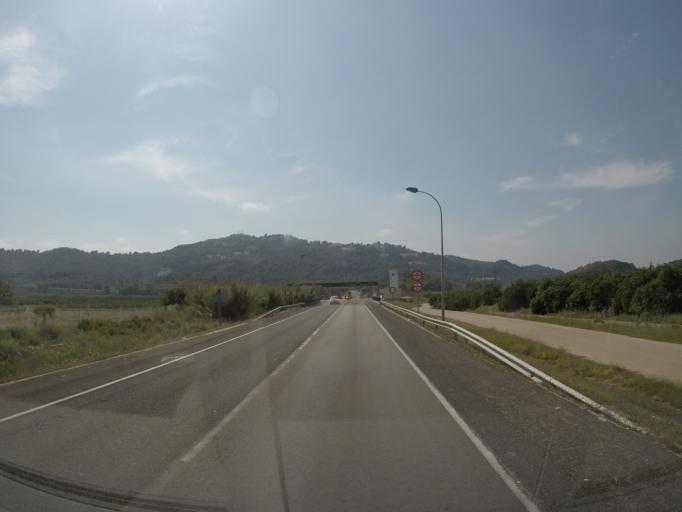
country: ES
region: Valencia
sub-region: Provincia de Valencia
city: Piles
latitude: 38.9274
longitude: -0.1363
